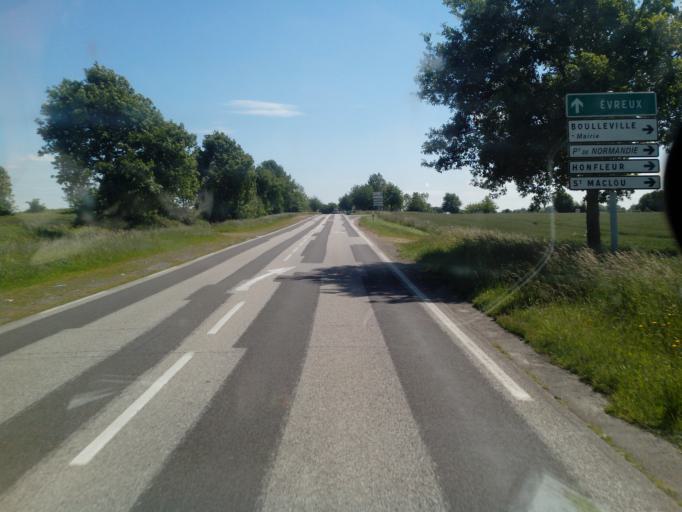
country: FR
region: Haute-Normandie
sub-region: Departement de l'Eure
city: Beuzeville
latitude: 49.3706
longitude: 0.3968
